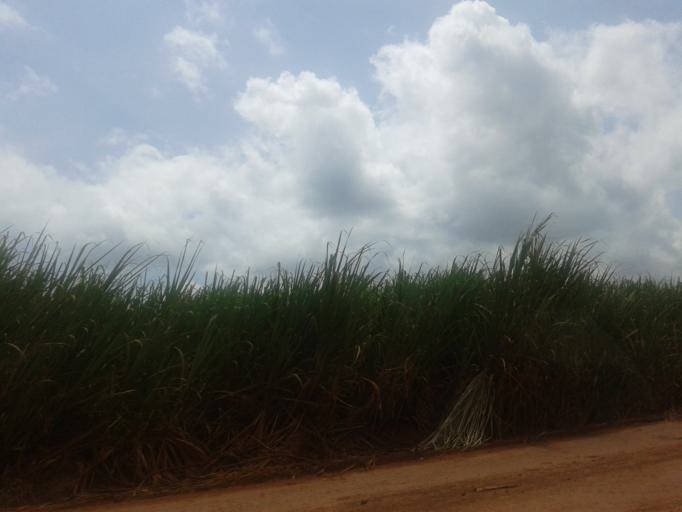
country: CM
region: Centre
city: Mbandjok
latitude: 4.4466
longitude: 11.9573
